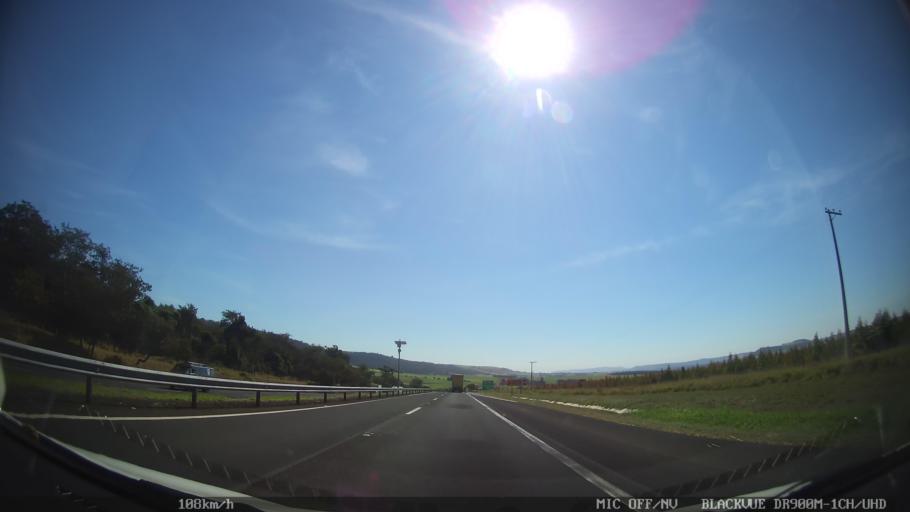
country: BR
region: Sao Paulo
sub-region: Sao Simao
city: Sao Simao
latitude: -21.5333
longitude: -47.6416
